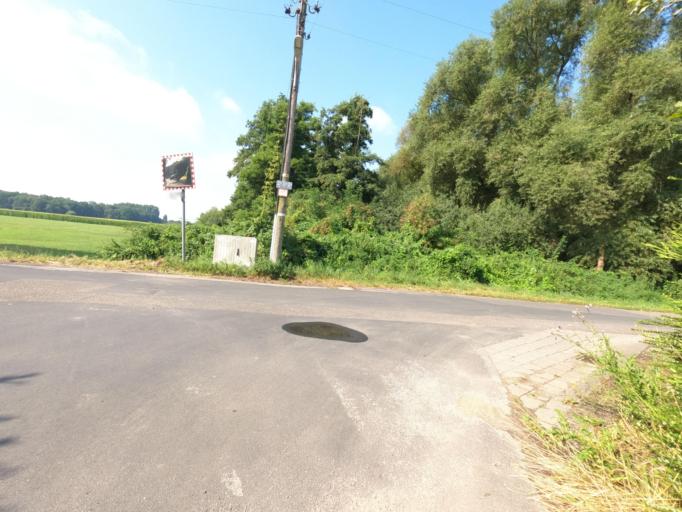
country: DE
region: North Rhine-Westphalia
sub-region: Regierungsbezirk Koln
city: Heinsberg
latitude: 51.0902
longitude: 6.0758
